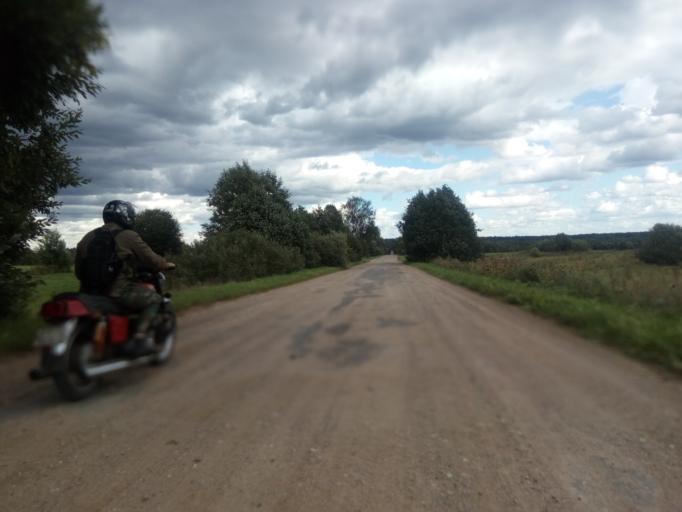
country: BY
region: Vitebsk
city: Dzisna
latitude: 55.7094
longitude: 28.3039
